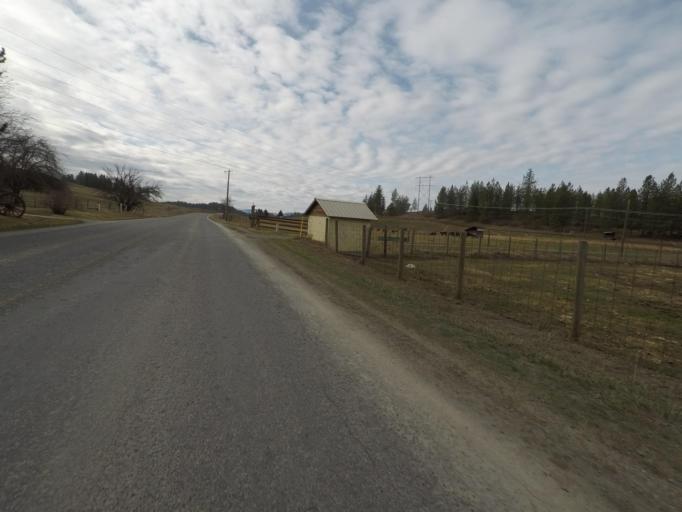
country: US
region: Washington
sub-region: Stevens County
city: Colville
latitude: 48.5266
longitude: -117.8807
